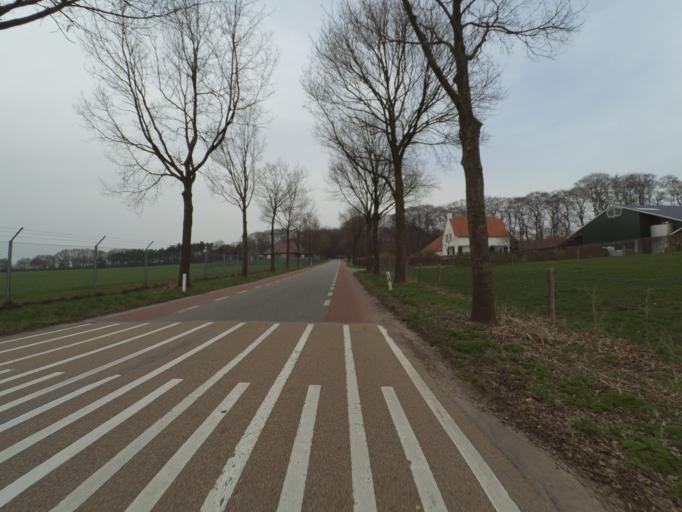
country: NL
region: Gelderland
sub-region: Gemeente Arnhem
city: Gulden Bodem
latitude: 52.0599
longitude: 5.8983
